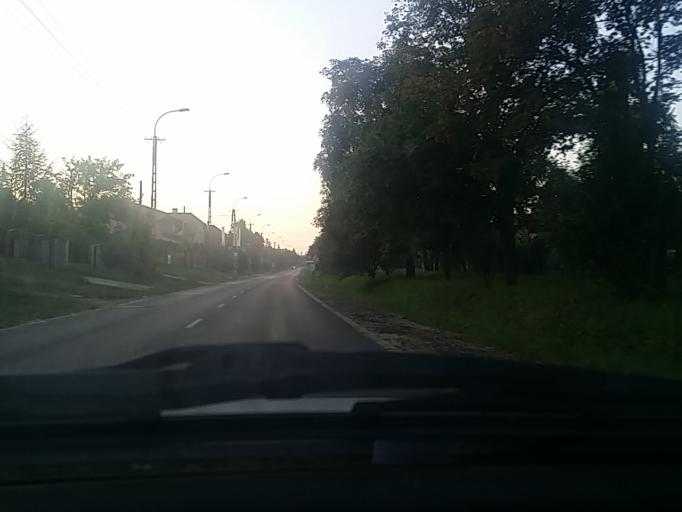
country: HU
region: Pest
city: Ecser
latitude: 47.4684
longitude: 19.3007
